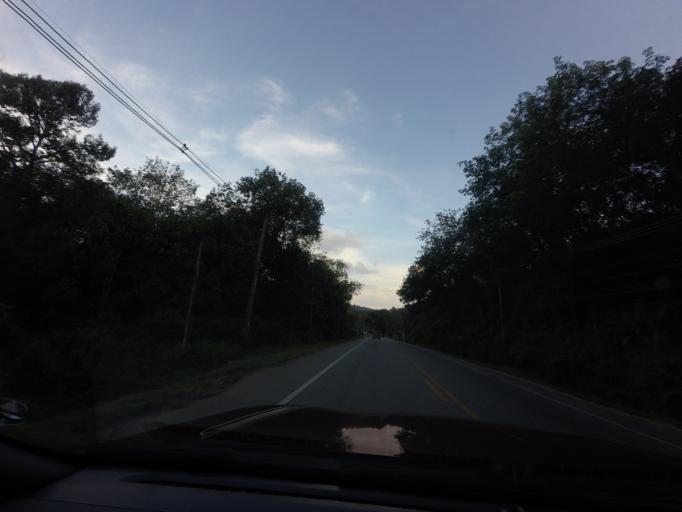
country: TH
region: Yala
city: Than To
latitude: 6.1310
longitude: 101.1919
